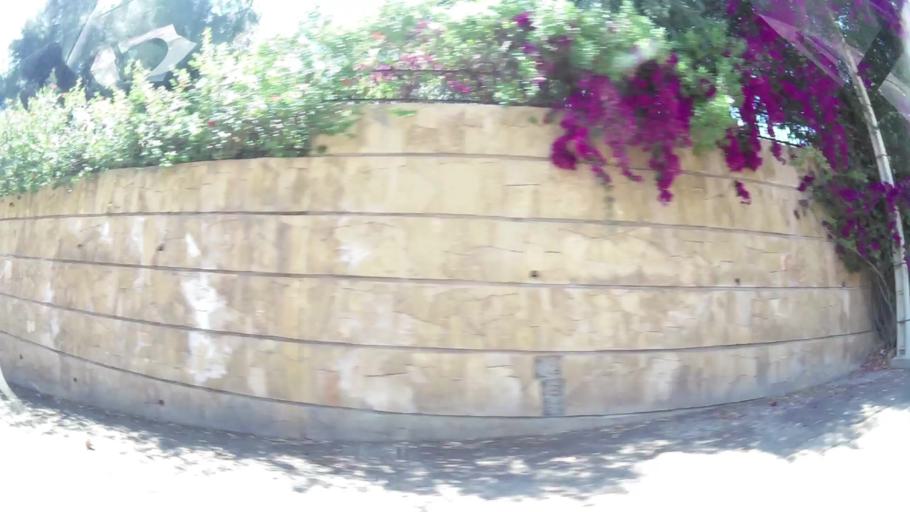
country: MA
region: Souss-Massa-Draa
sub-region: Agadir-Ida-ou-Tnan
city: Agadir
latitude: 30.4277
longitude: -9.5972
